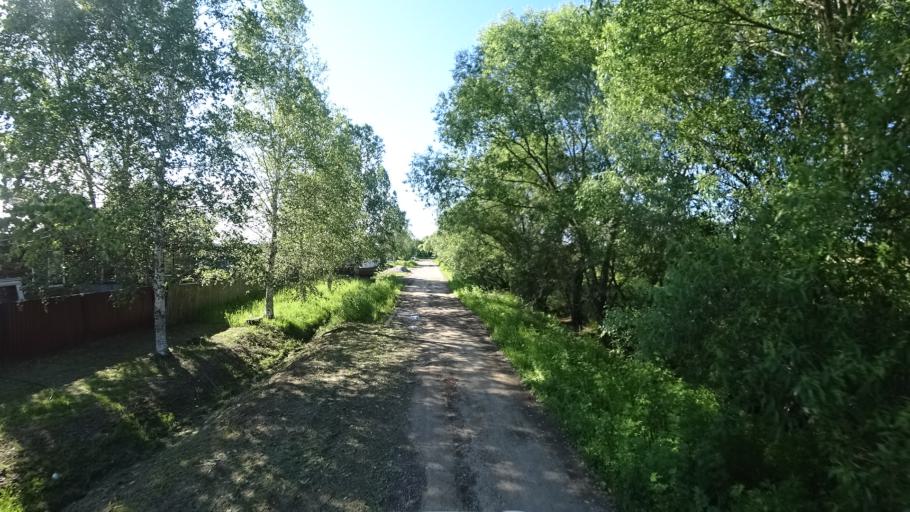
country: RU
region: Khabarovsk Krai
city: Khor
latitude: 47.8943
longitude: 134.9960
